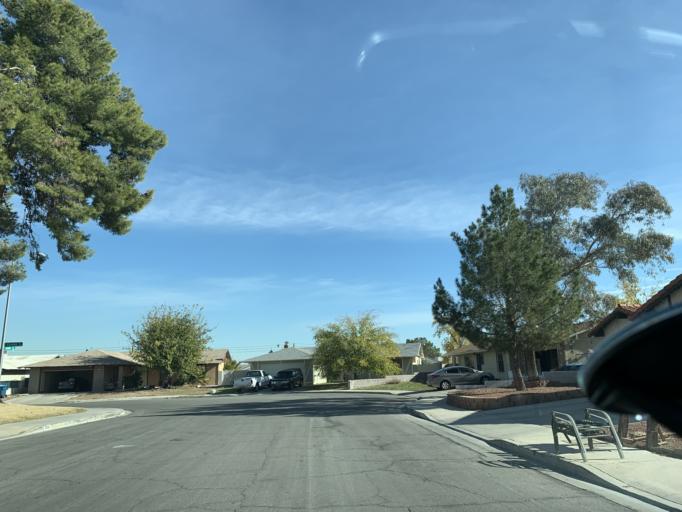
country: US
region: Nevada
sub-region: Clark County
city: Spring Valley
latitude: 36.1041
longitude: -115.2271
